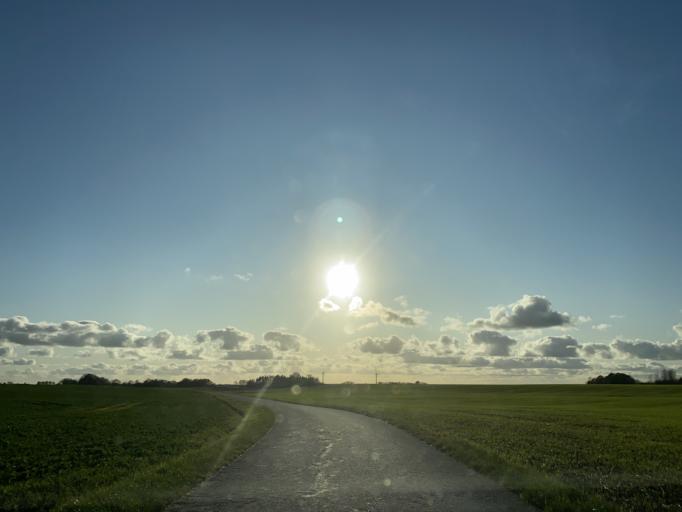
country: DK
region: Central Jutland
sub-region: Viborg Kommune
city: Bjerringbro
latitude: 56.3466
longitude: 9.7168
